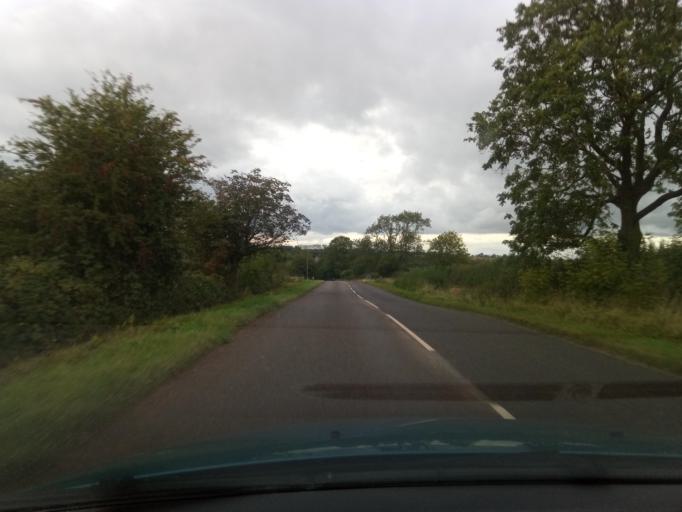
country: GB
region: England
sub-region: Leicestershire
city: Sileby
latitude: 52.7472
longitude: -1.0743
